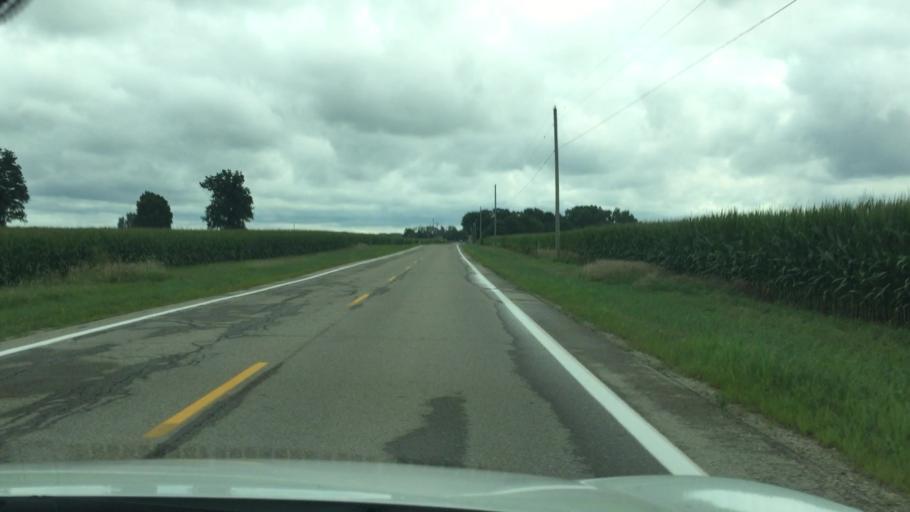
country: US
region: Ohio
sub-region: Champaign County
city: Mechanicsburg
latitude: 40.1471
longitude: -83.5292
